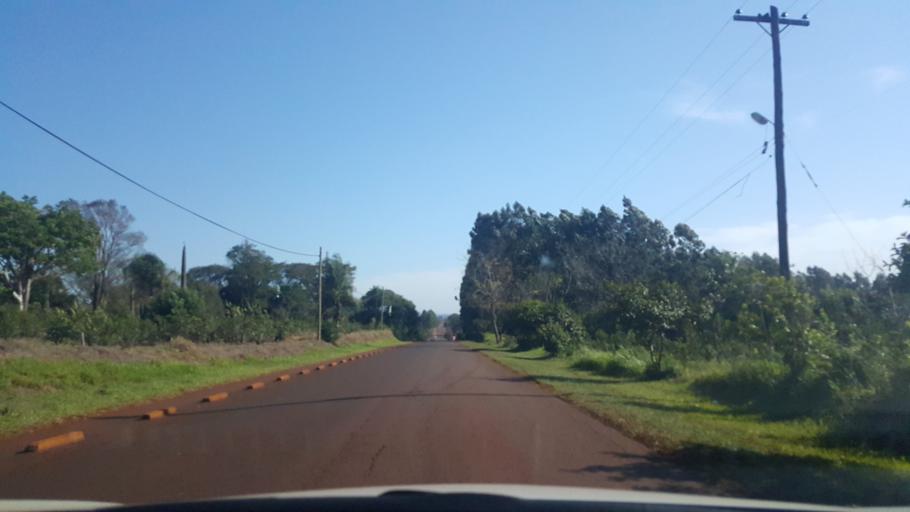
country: AR
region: Misiones
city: Santo Pipo
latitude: -27.1457
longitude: -55.4010
